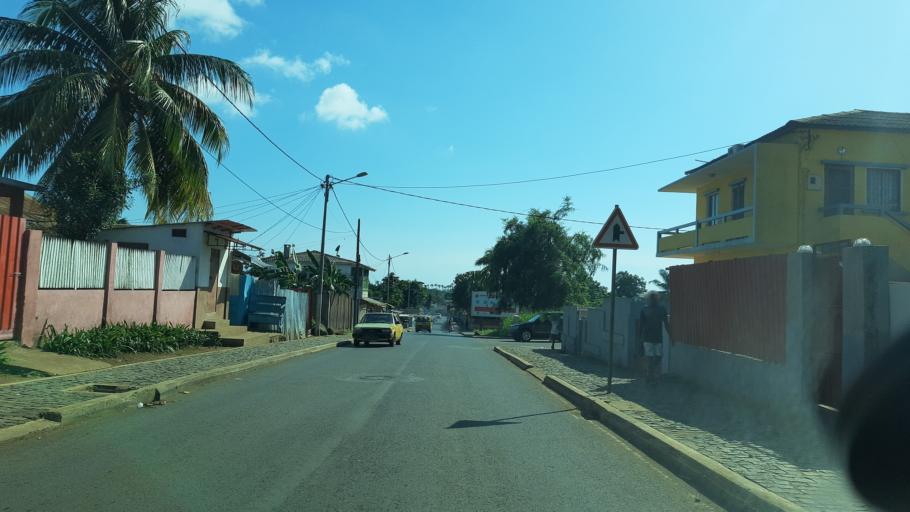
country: ST
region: Sao Tome Island
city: Sao Tome
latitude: 0.3282
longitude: 6.7293
